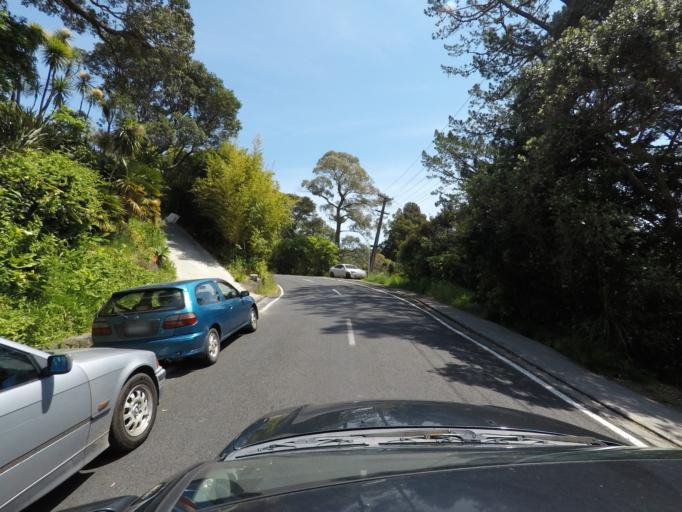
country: NZ
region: Auckland
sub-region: Auckland
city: Titirangi
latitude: -36.9687
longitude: 174.6396
